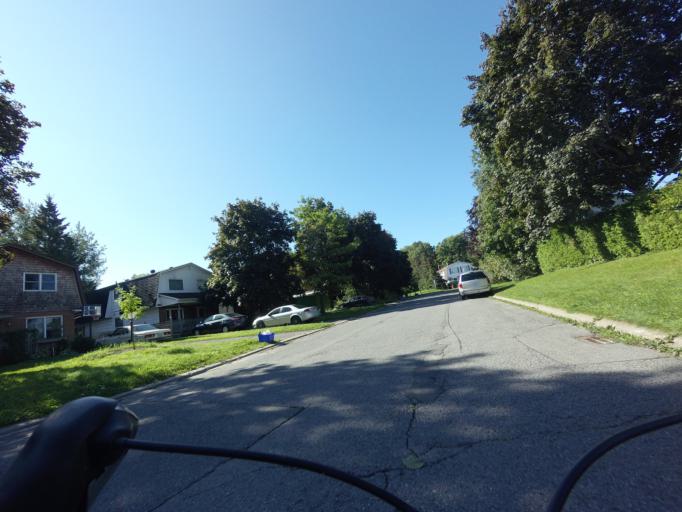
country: CA
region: Ontario
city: Bells Corners
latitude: 45.3156
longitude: -75.8399
